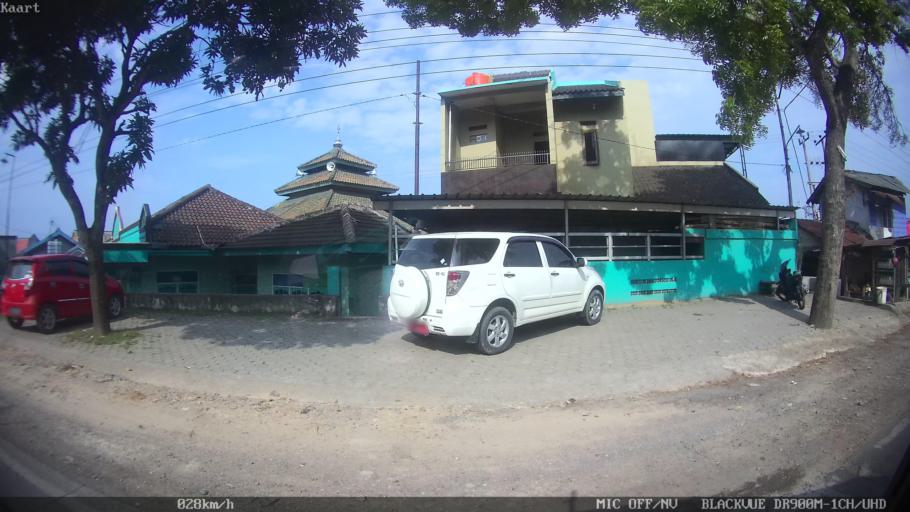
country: ID
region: Lampung
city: Panjang
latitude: -5.4709
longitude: 105.3242
